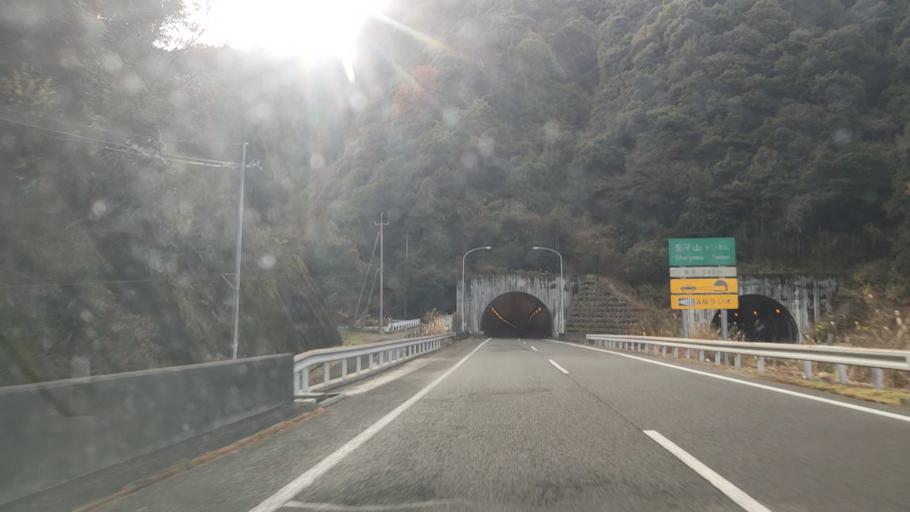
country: JP
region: Ehime
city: Niihama
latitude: 33.9222
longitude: 133.3173
